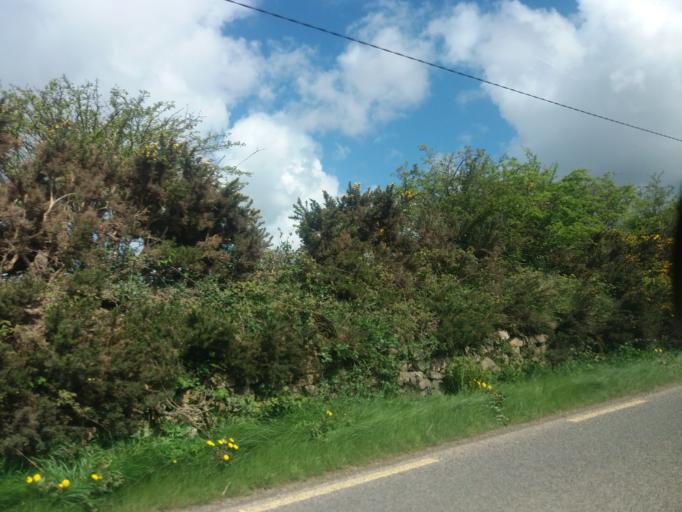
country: IE
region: Leinster
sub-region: Loch Garman
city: Loch Garman
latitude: 52.2902
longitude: -6.5897
